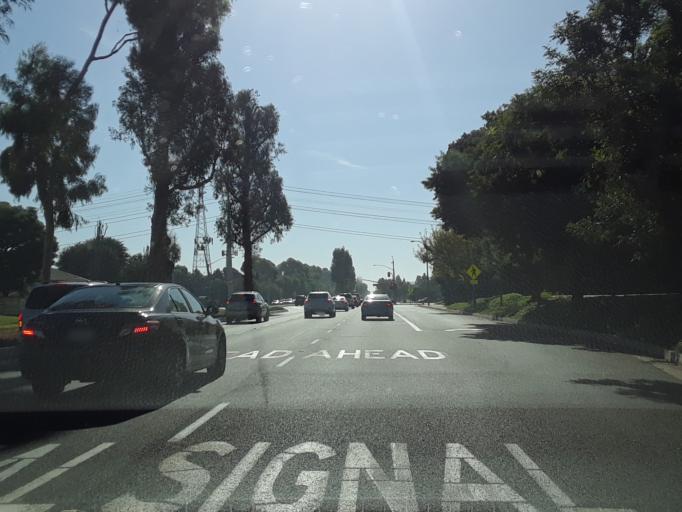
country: US
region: California
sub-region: Orange County
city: Irvine
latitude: 33.6805
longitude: -117.7804
